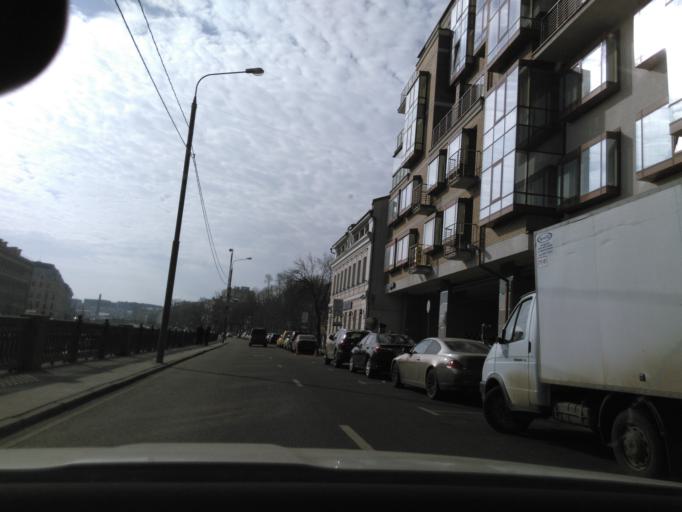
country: RU
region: Moscow
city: Zamoskvorech'ye
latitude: 55.7393
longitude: 37.6385
